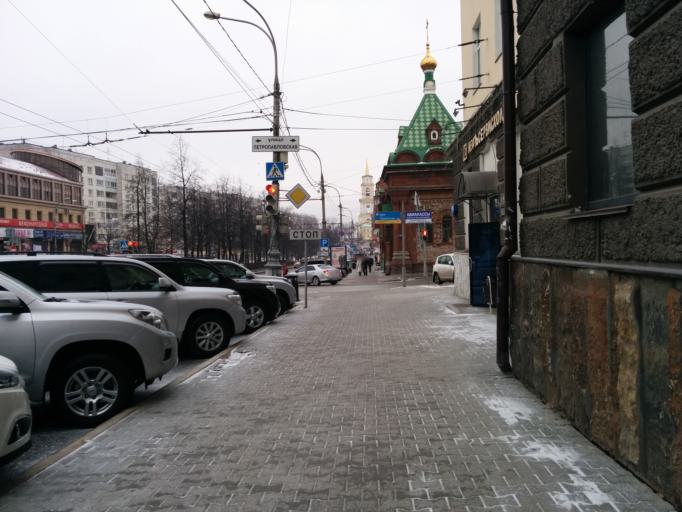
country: RU
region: Perm
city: Perm
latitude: 58.0125
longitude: 56.2381
